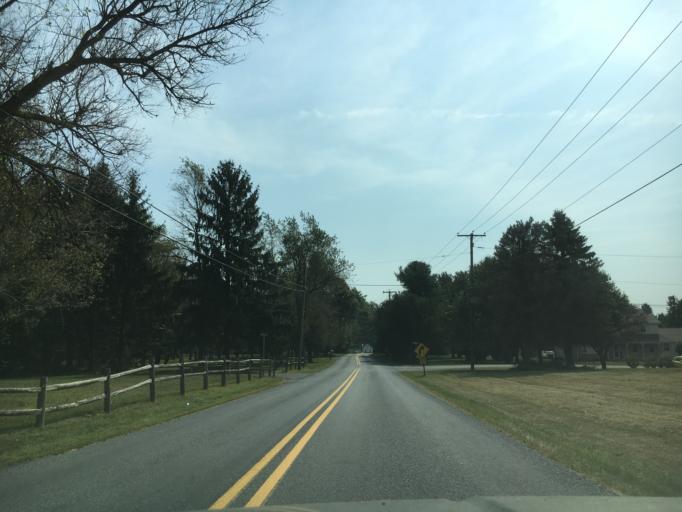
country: US
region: Pennsylvania
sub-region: Berks County
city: Topton
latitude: 40.5674
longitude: -75.7061
